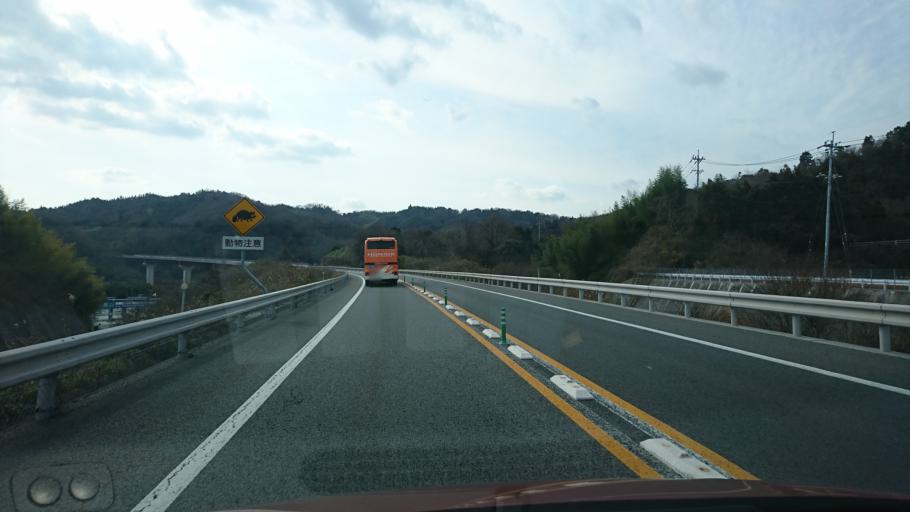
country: JP
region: Hiroshima
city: Innoshima
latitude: 34.1702
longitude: 133.0651
